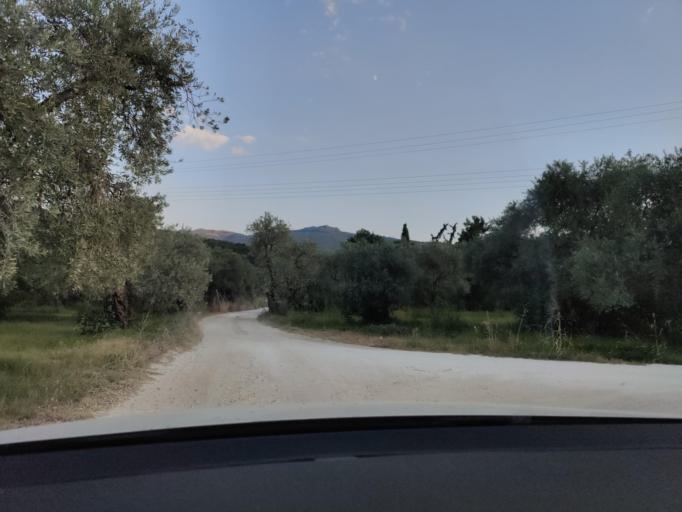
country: GR
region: East Macedonia and Thrace
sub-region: Nomos Kavalas
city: Prinos
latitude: 40.7484
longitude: 24.5744
